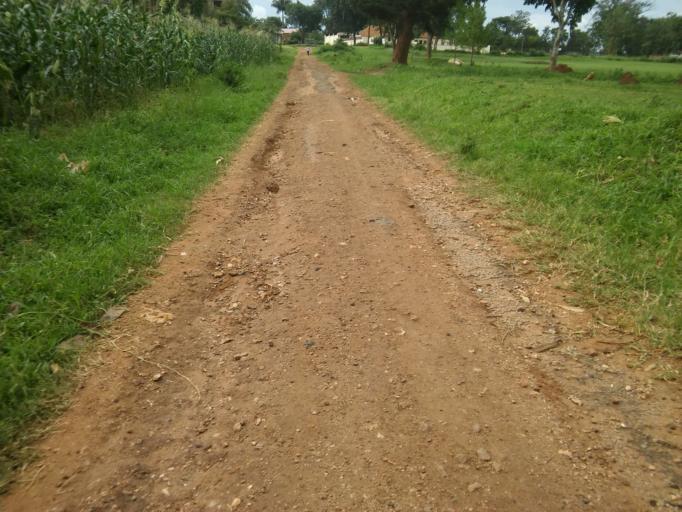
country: UG
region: Eastern Region
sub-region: Mbale District
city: Mbale
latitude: 1.0663
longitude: 34.1848
